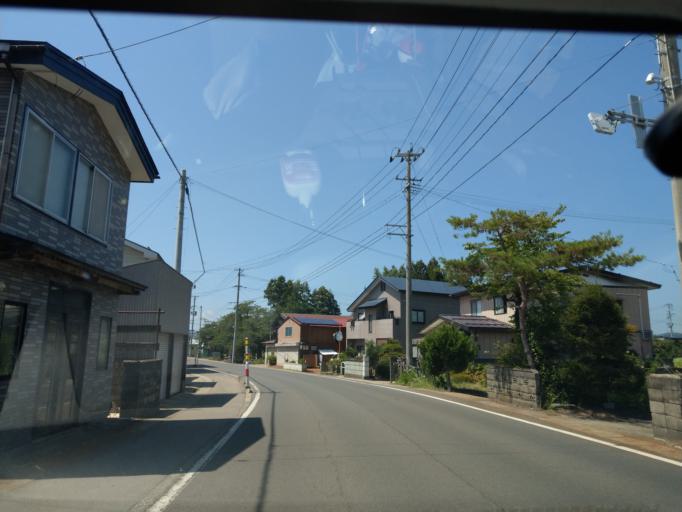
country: JP
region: Akita
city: Yokotemachi
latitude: 39.3201
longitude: 140.5416
